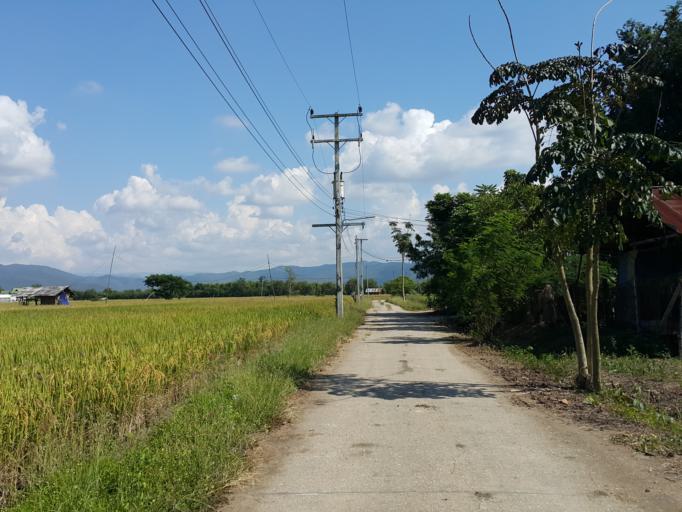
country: TH
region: Chiang Mai
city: San Kamphaeng
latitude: 18.7897
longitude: 99.1411
